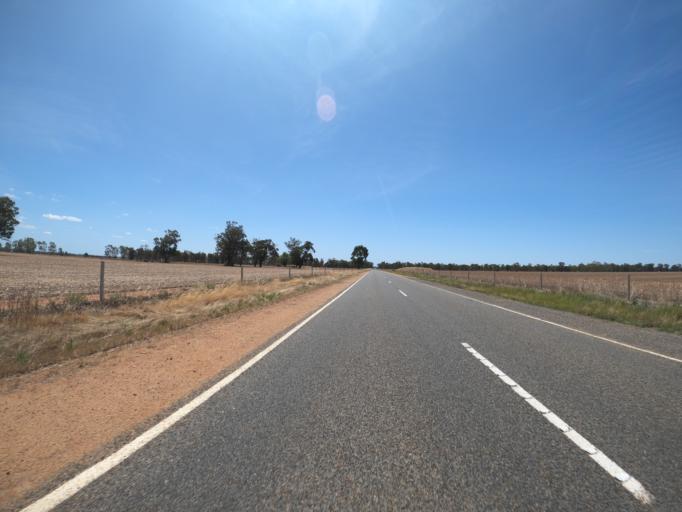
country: AU
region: Victoria
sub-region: Moira
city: Yarrawonga
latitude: -36.1658
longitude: 145.9672
